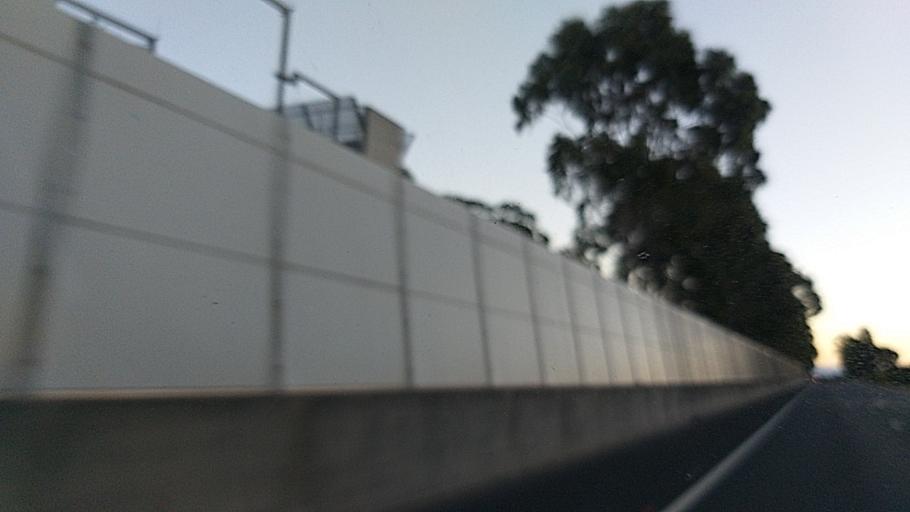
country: AU
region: New South Wales
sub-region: Blacktown
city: Glendenning
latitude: -33.7636
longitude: 150.8462
